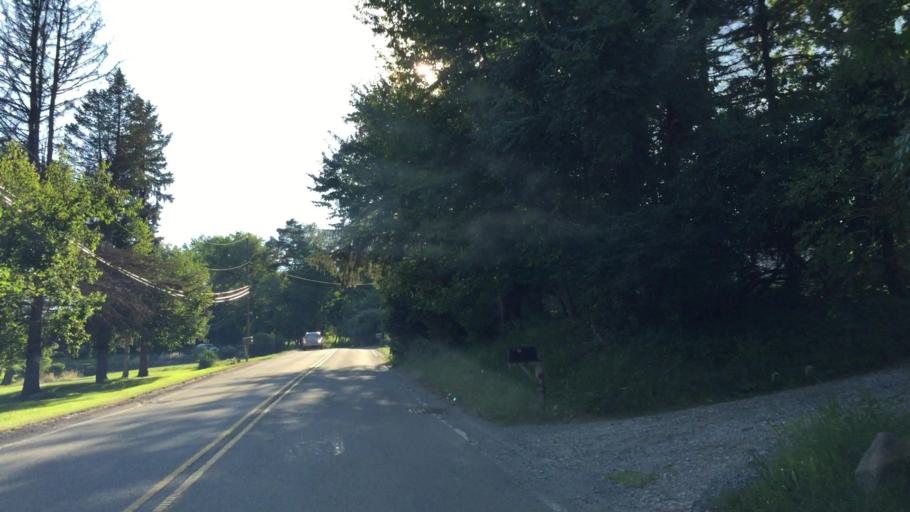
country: US
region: Pennsylvania
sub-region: Allegheny County
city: Franklin Park
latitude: 40.5876
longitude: -80.0525
